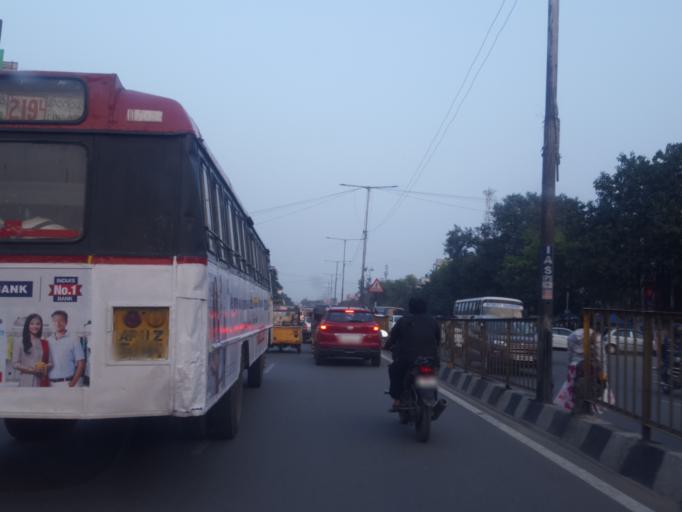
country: IN
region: Telangana
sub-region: Medak
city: Serilingampalle
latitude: 17.4949
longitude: 78.3220
